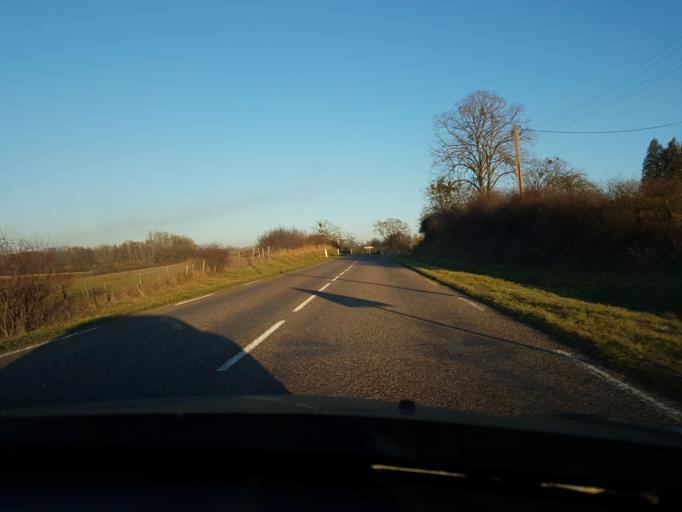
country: FR
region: Lorraine
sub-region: Departement des Vosges
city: Darney
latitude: 47.9332
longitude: 6.0682
